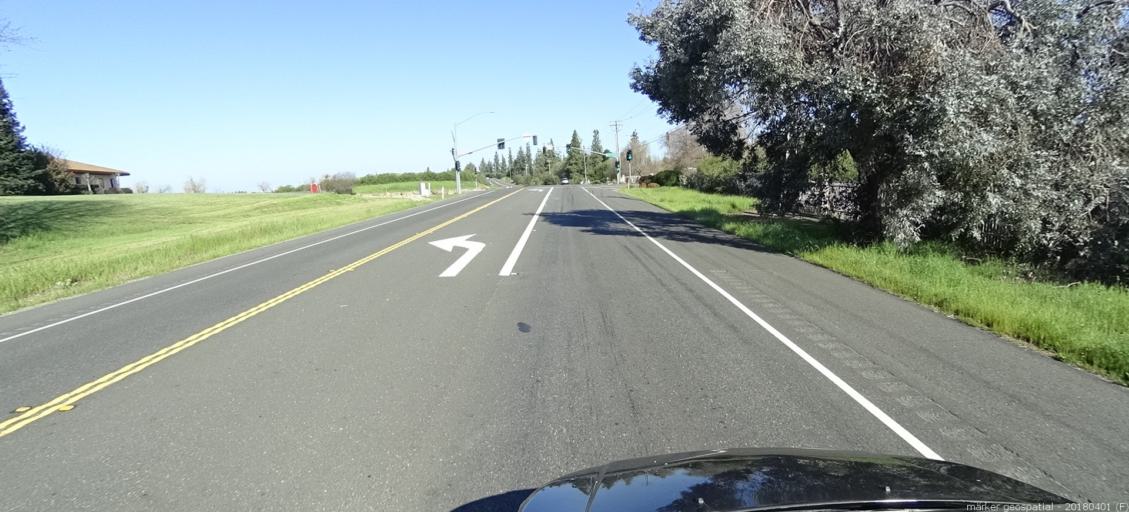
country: US
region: California
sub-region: Sacramento County
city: Rancho Murieta
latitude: 38.4869
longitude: -121.0821
